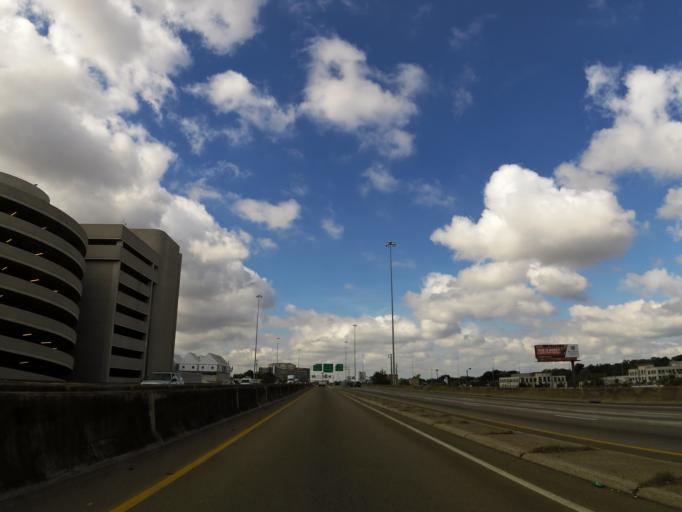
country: US
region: Alabama
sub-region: Jefferson County
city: Birmingham
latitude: 33.5226
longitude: -86.8116
